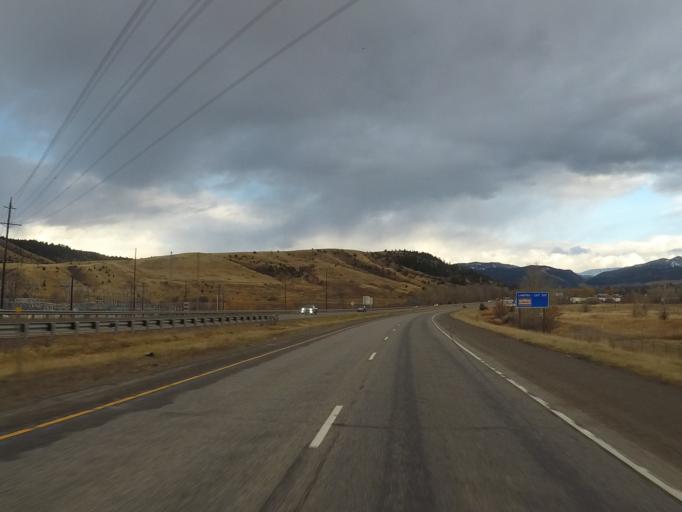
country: US
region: Montana
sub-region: Gallatin County
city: Bozeman
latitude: 45.6913
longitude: -111.0239
